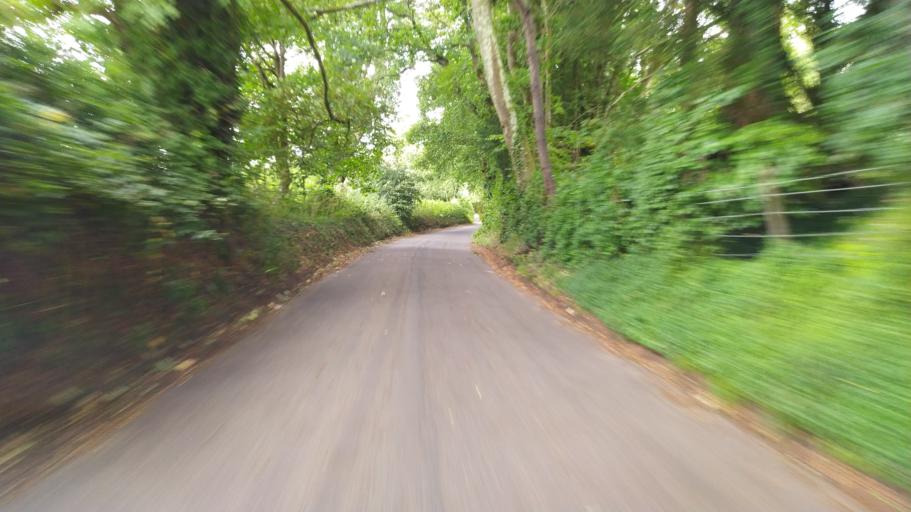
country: GB
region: England
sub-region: Dorset
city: Broadstone
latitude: 50.7755
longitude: -2.0358
